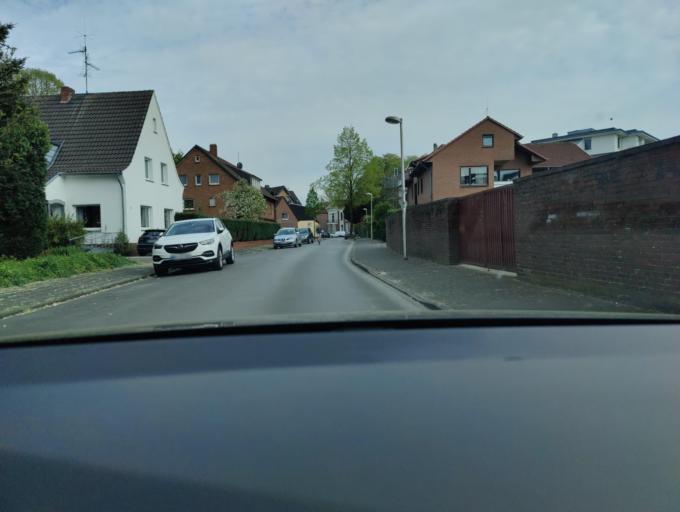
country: DE
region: North Rhine-Westphalia
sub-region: Regierungsbezirk Munster
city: Gronau
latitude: 52.2138
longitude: 7.0153
